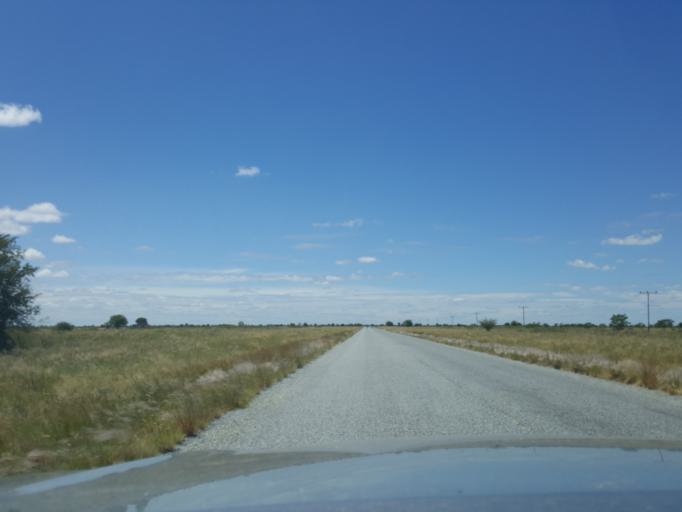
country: BW
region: Central
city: Nata
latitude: -20.2002
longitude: 26.1166
